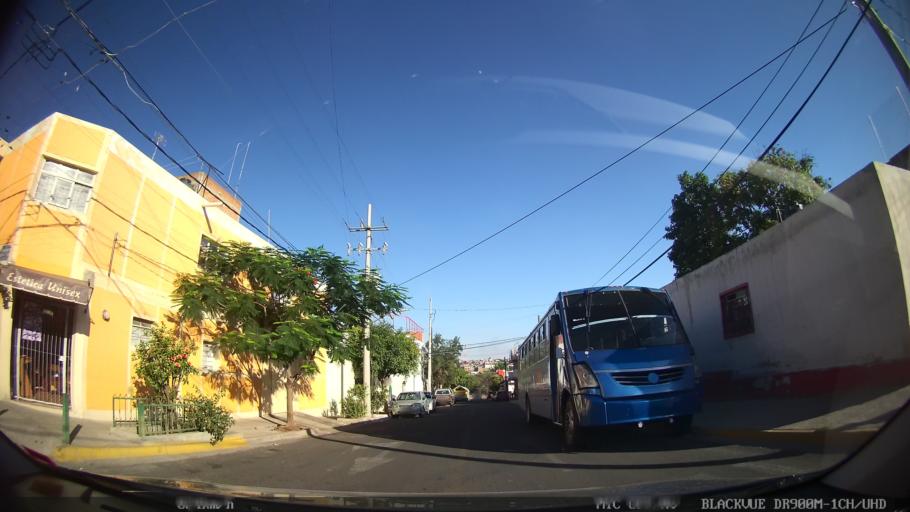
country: MX
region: Jalisco
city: Tlaquepaque
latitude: 20.7061
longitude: -103.2878
